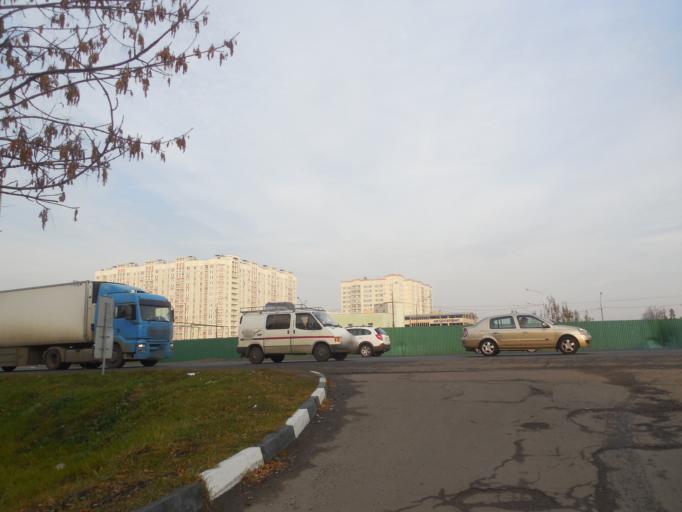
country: RU
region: Moskovskaya
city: Shcherbinka
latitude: 55.5003
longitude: 37.5707
